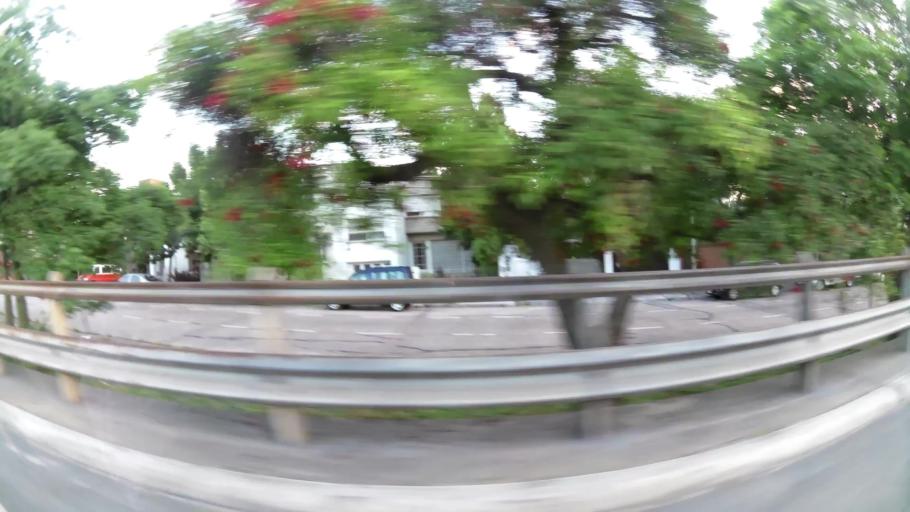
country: AR
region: Buenos Aires
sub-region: Partido de Vicente Lopez
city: Olivos
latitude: -34.5421
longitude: -58.4817
